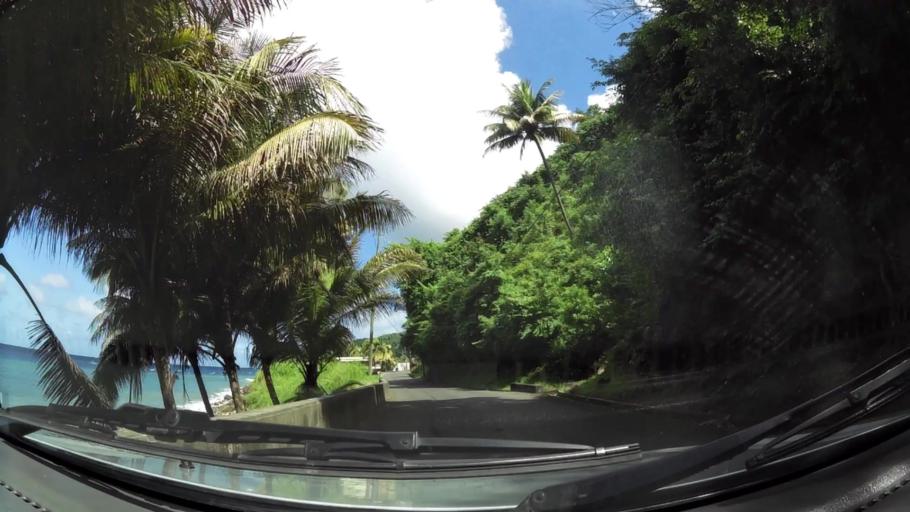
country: GD
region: Saint Mark
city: Victoria
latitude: 12.1942
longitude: -61.7088
